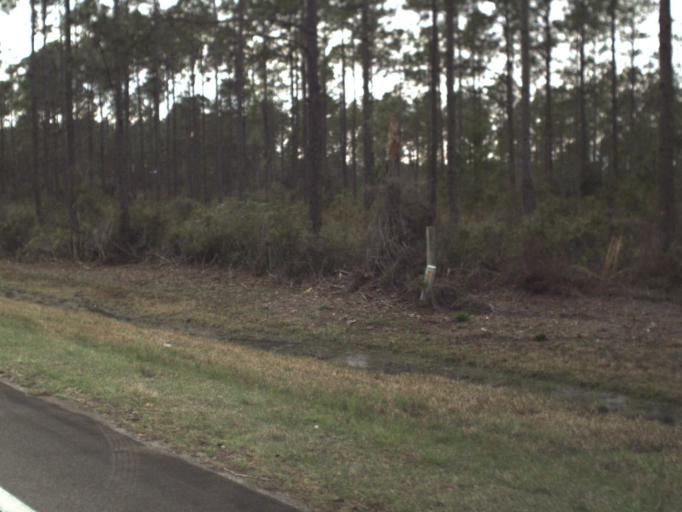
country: US
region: Florida
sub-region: Gulf County
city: Wewahitchka
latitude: 30.1335
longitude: -85.3435
